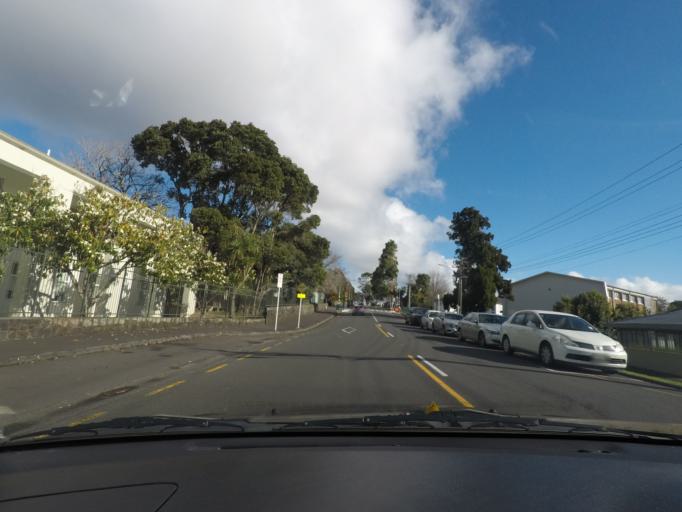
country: NZ
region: Auckland
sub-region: Auckland
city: Auckland
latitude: -36.8868
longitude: 174.7786
